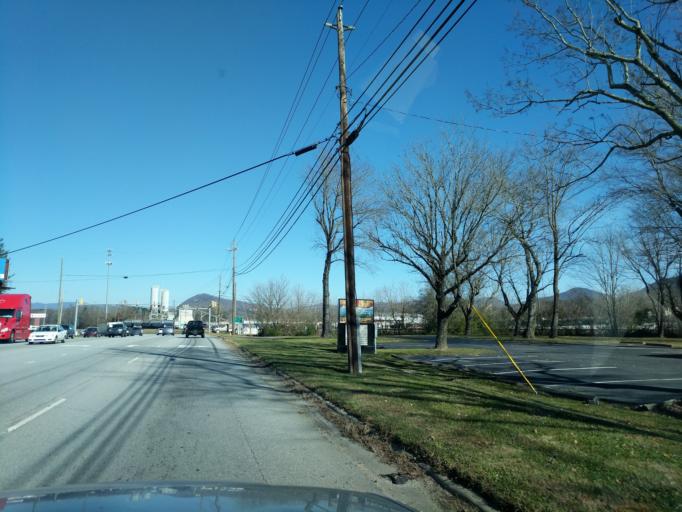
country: US
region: North Carolina
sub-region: Henderson County
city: Fletcher
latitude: 35.4135
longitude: -82.5090
